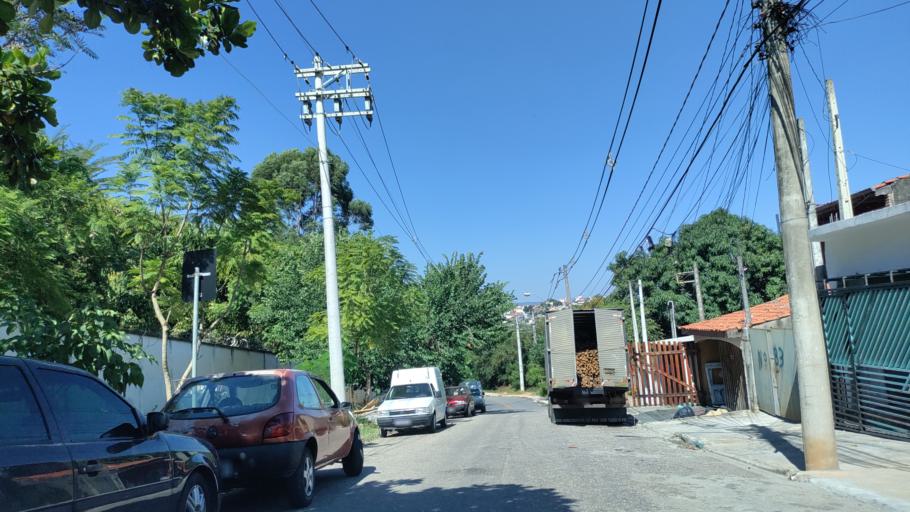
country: BR
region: Sao Paulo
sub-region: Sorocaba
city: Sorocaba
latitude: -23.4675
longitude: -47.4703
